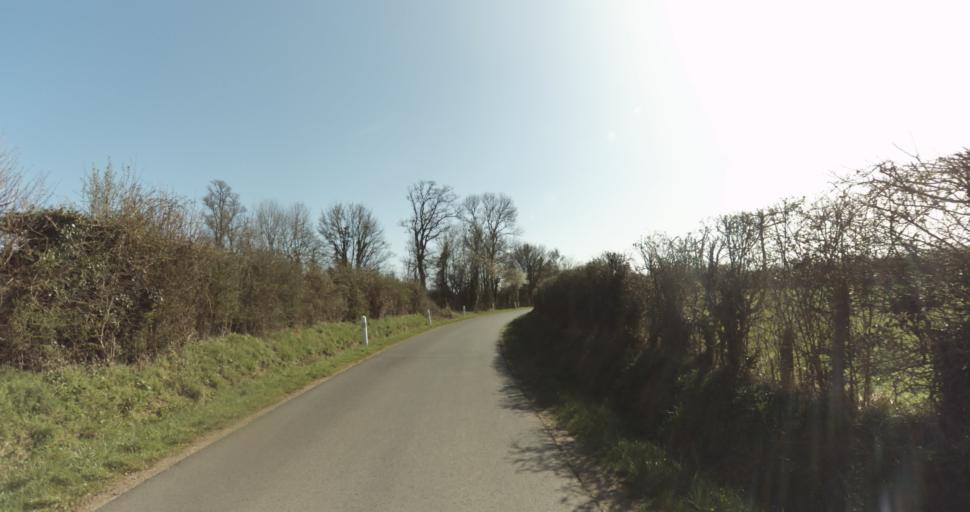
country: FR
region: Lower Normandy
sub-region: Departement de l'Orne
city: Trun
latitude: 48.8973
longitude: 0.0330
